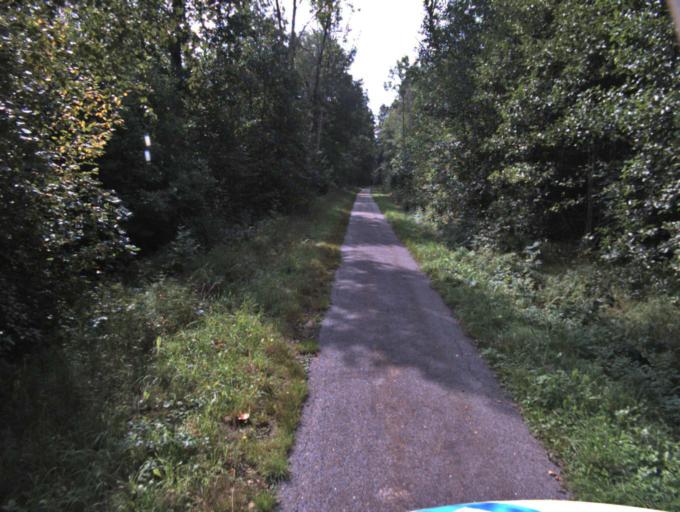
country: SE
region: Vaestra Goetaland
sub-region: Tranemo Kommun
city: Limmared
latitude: 57.6352
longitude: 13.3536
